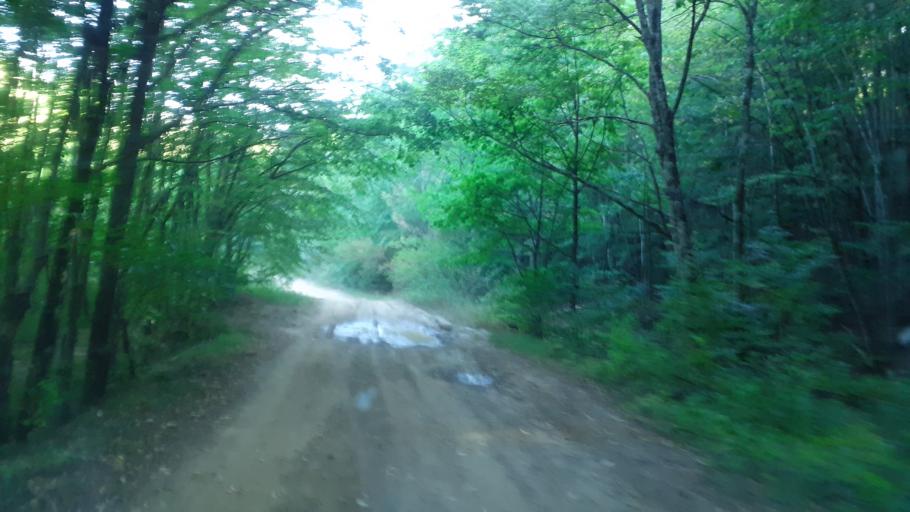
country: RU
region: Krasnodarskiy
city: Azovskaya
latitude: 44.6686
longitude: 38.5018
